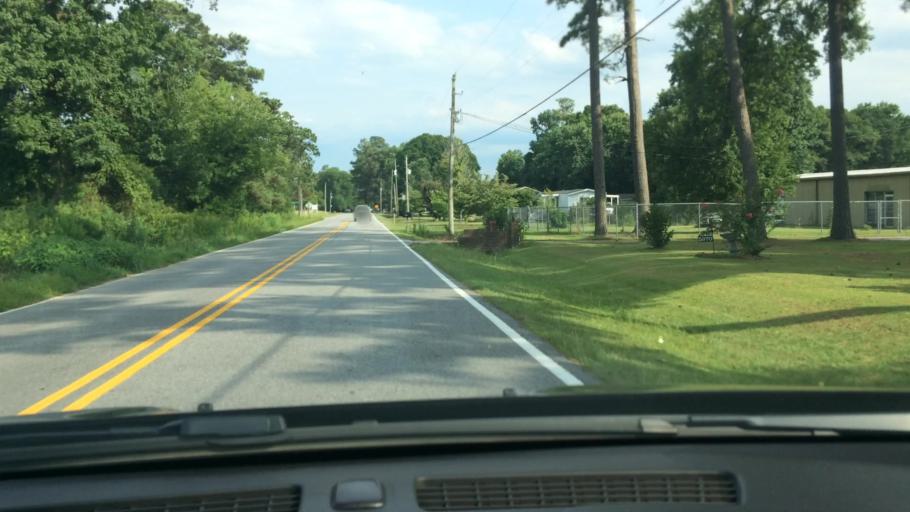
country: US
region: North Carolina
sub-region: Pitt County
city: Ayden
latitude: 35.4912
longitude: -77.3772
